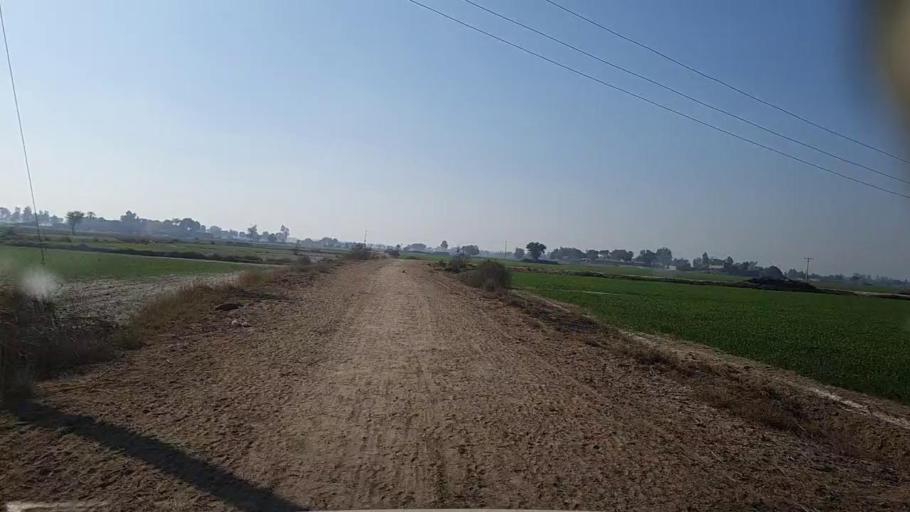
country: PK
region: Sindh
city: Khairpur
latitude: 27.9308
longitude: 69.6951
